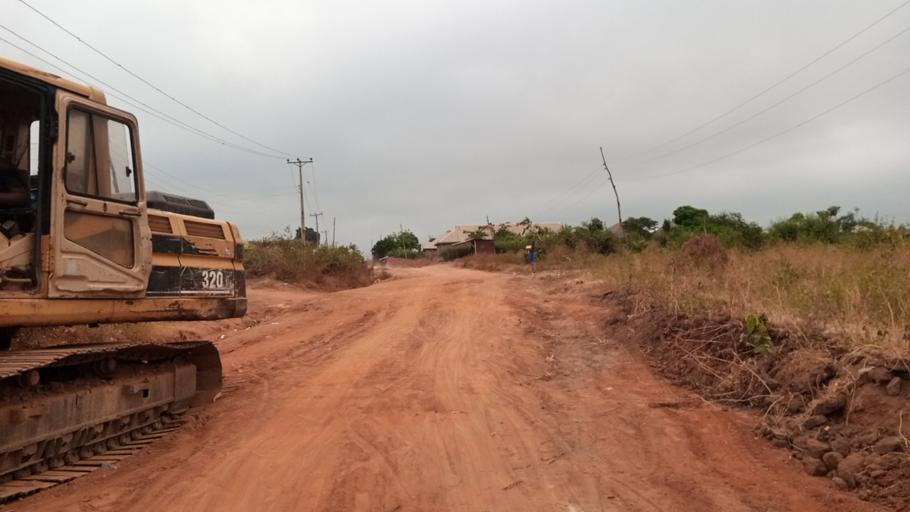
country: NG
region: Osun
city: Osogbo
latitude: 7.7620
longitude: 4.6246
